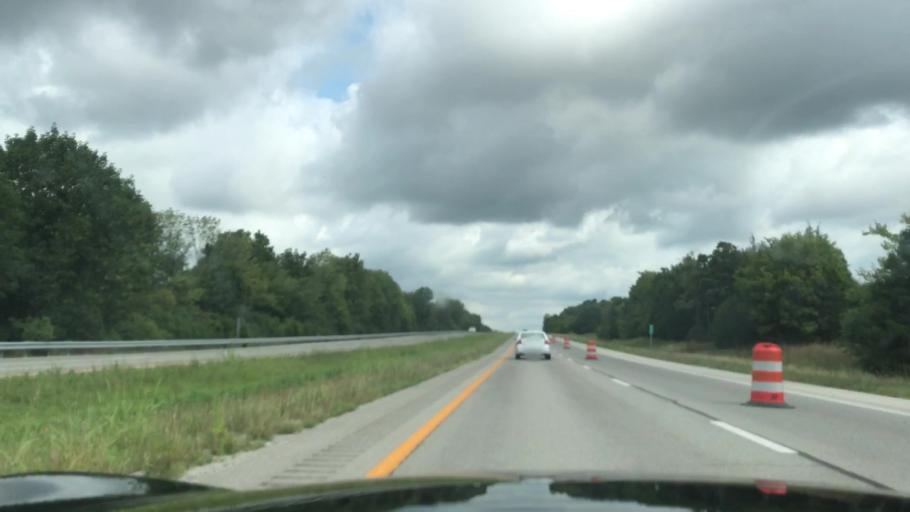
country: US
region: Kentucky
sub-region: Butler County
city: Morgantown
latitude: 37.1076
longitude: -86.6404
